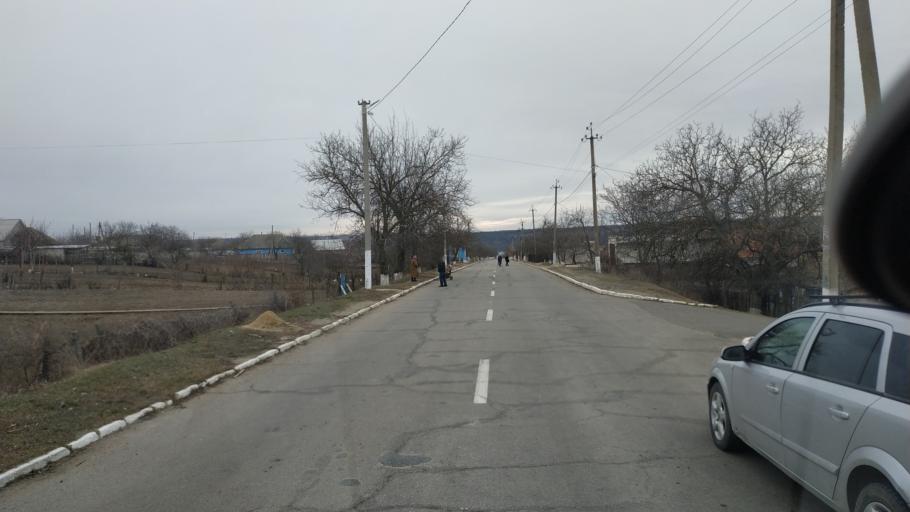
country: MD
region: Telenesti
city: Cocieri
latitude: 47.3530
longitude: 29.1168
